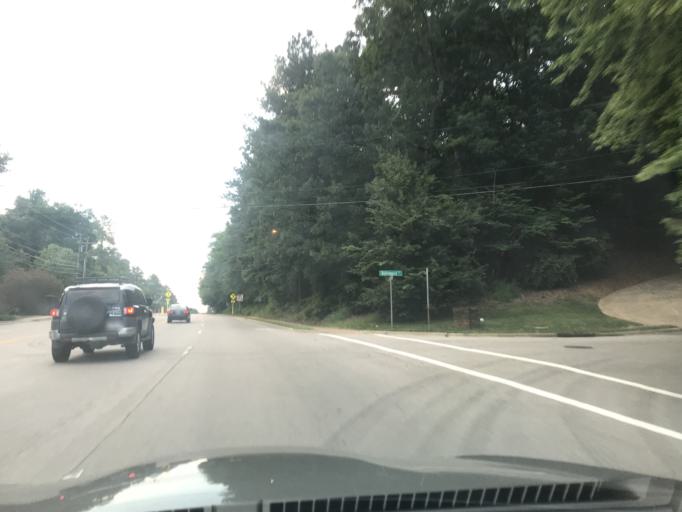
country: US
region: North Carolina
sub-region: Orange County
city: Chapel Hill
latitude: 35.9272
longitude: -79.0538
